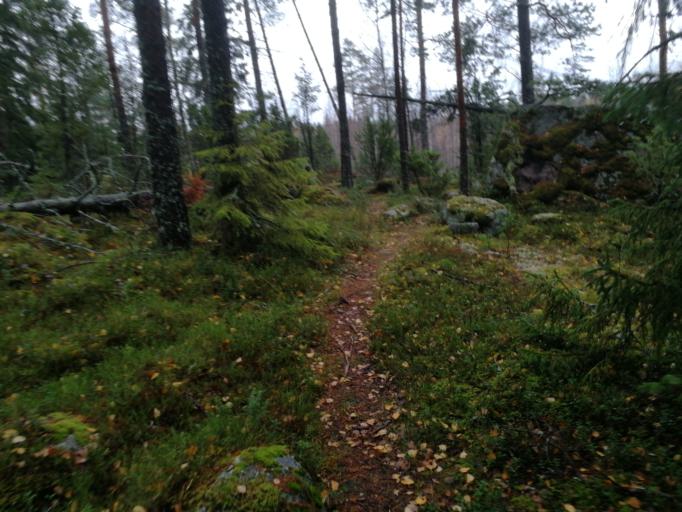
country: FI
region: Pirkanmaa
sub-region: Tampere
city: Tampere
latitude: 61.4566
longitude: 23.8773
